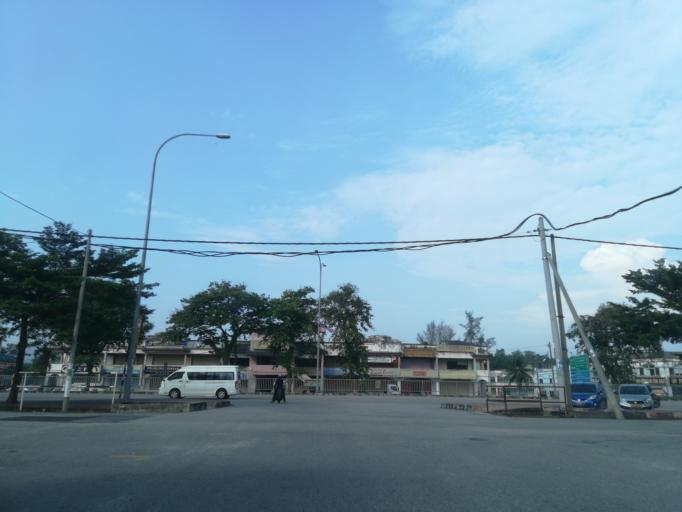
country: MY
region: Kedah
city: Kulim
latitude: 5.3891
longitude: 100.5657
